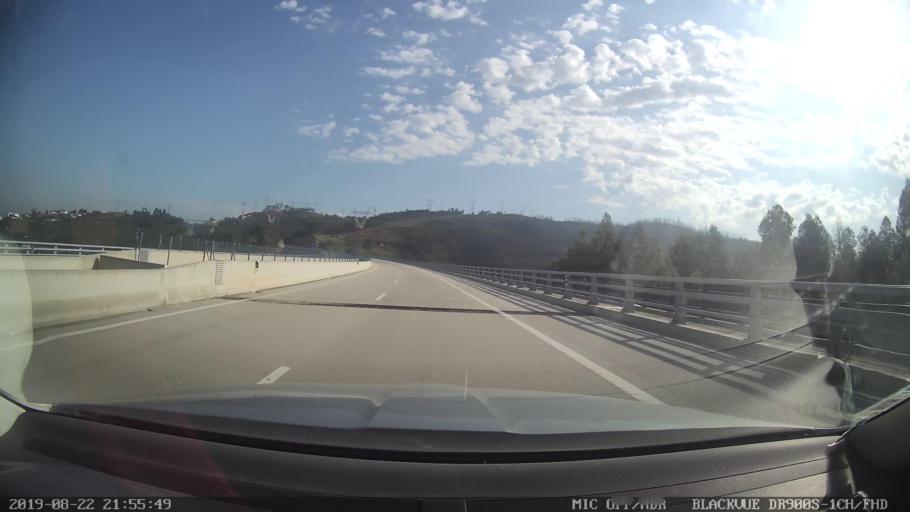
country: PT
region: Coimbra
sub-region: Coimbra
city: Coimbra
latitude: 40.1594
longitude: -8.3796
